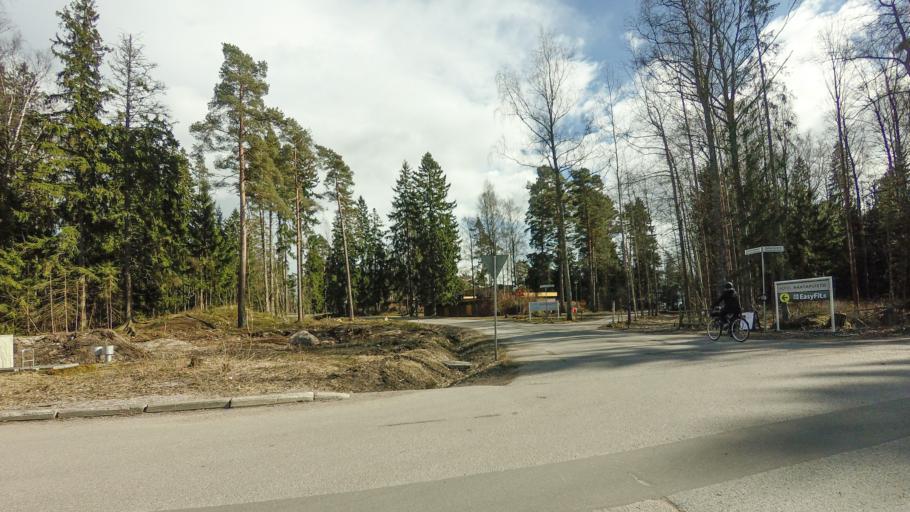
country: FI
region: Uusimaa
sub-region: Helsinki
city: Vantaa
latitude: 60.1964
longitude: 25.1117
